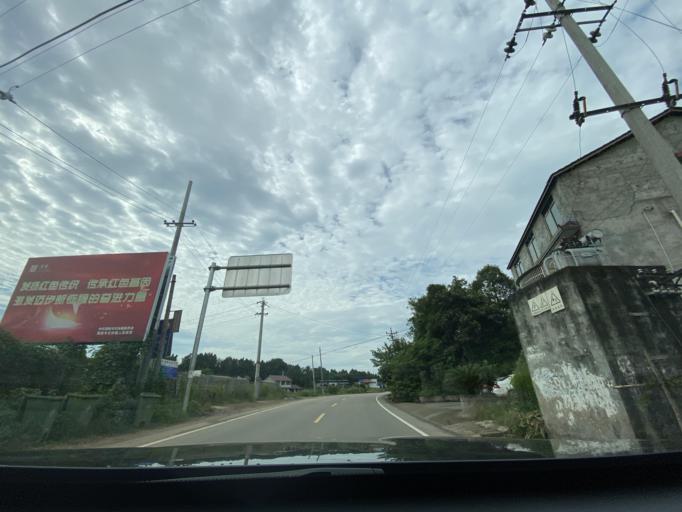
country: CN
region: Sichuan
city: Jiancheng
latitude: 30.4624
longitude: 104.6297
